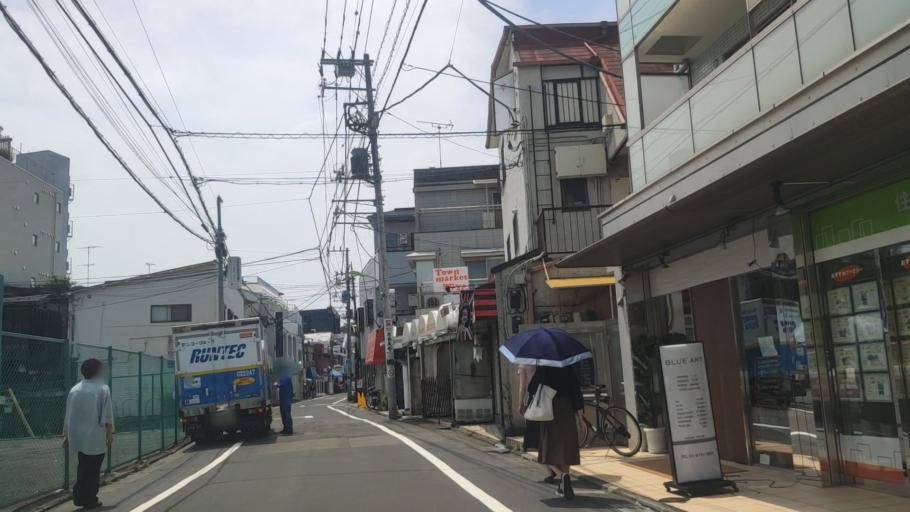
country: JP
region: Tokyo
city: Tokyo
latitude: 35.6634
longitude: 139.6655
